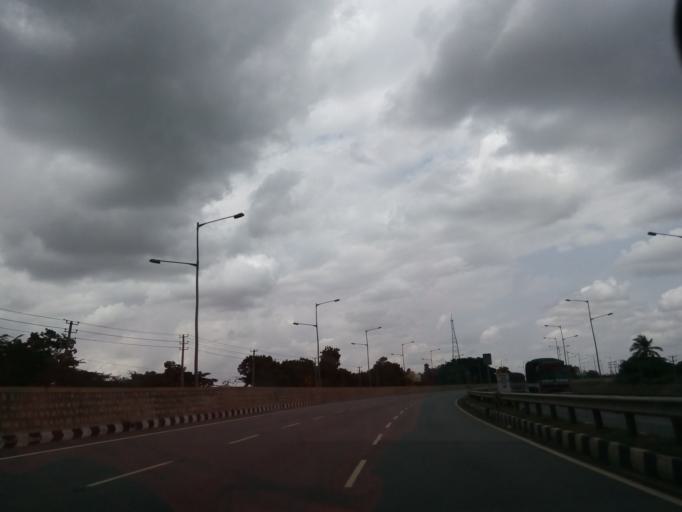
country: IN
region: Karnataka
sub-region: Chitradurga
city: Hiriyur
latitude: 13.9581
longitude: 76.6175
